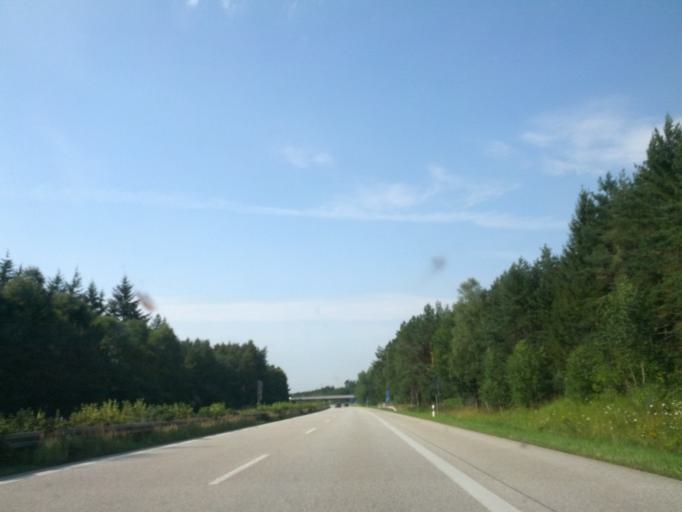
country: DE
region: Mecklenburg-Vorpommern
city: Lalendorf
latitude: 53.7689
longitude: 12.3235
